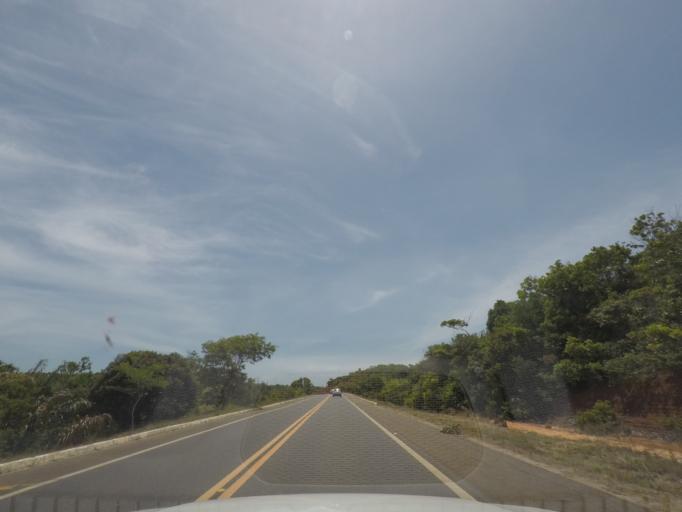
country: BR
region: Bahia
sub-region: Mata De Sao Joao
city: Mata de Sao Joao
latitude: -12.4694
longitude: -37.9596
